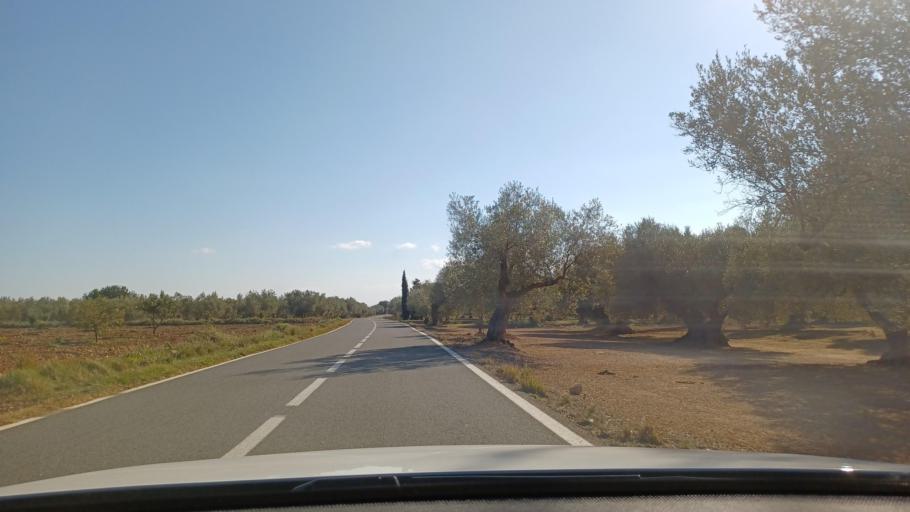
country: ES
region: Catalonia
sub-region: Provincia de Tarragona
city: Mas de Barberans
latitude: 40.6378
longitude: 0.3558
